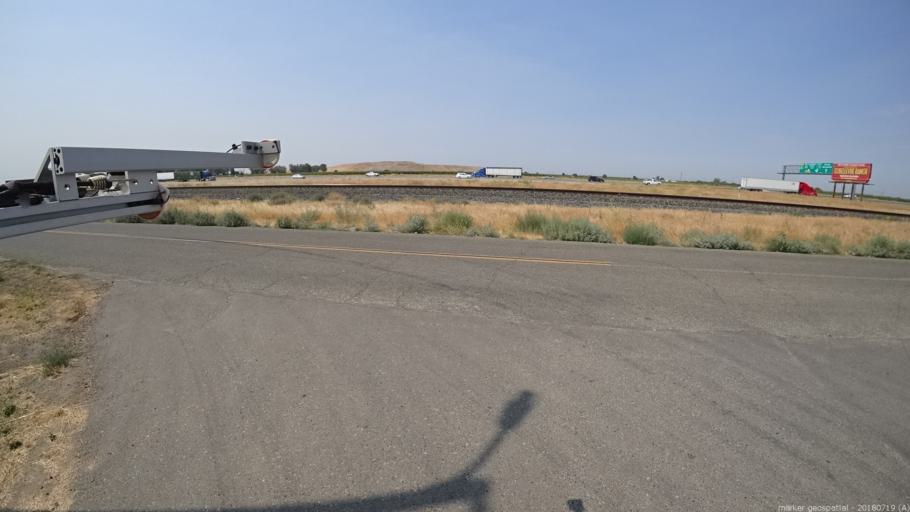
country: US
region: California
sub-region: Madera County
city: Fairmead
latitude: 37.0745
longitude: -120.1952
